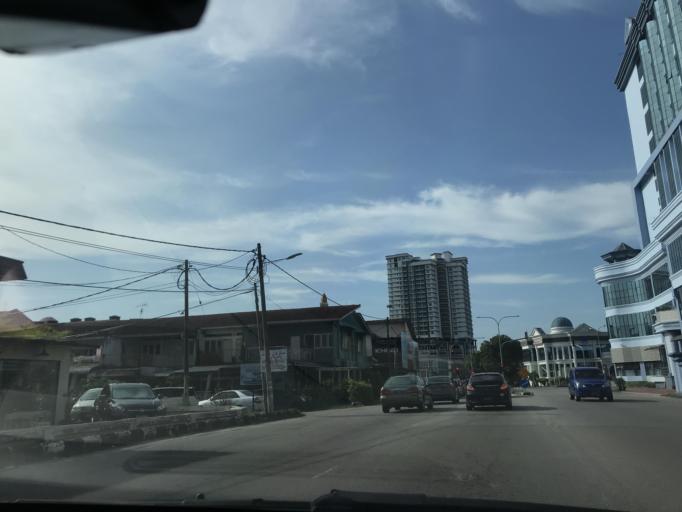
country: MY
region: Kelantan
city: Kota Bharu
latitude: 6.1264
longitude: 102.2473
